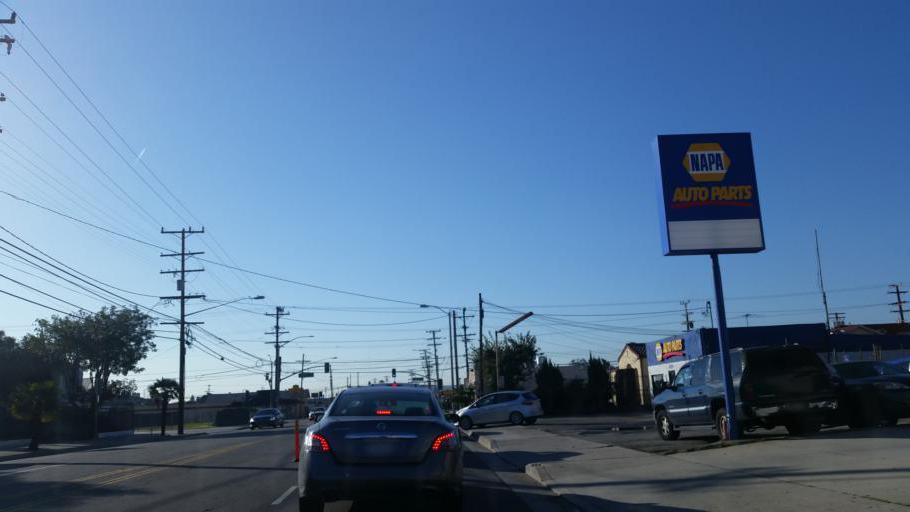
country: US
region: California
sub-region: Los Angeles County
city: Gardena
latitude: 33.8812
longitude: -118.2998
